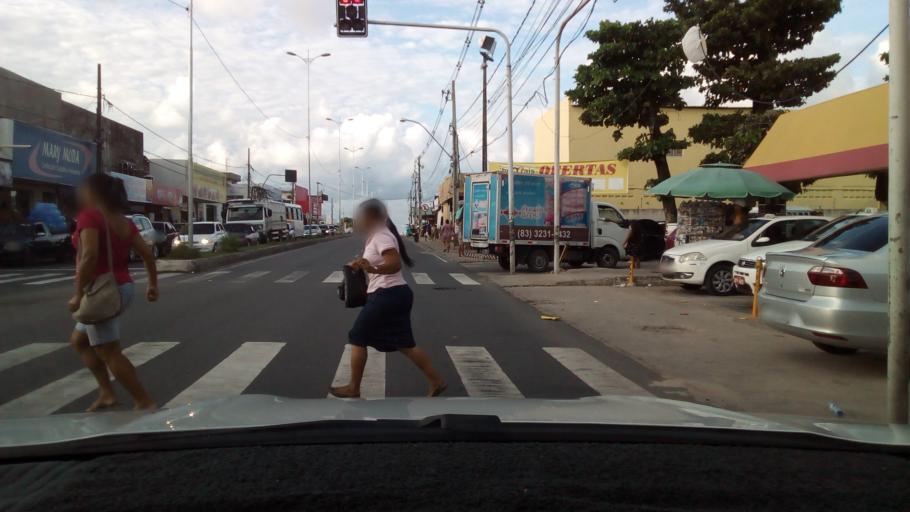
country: BR
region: Paraiba
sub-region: Bayeux
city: Bayeux
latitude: -7.1585
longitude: -34.8962
